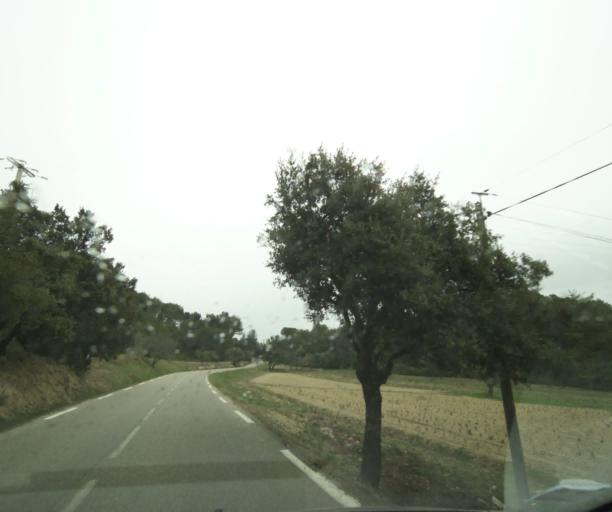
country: FR
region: Provence-Alpes-Cote d'Azur
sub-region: Departement des Bouches-du-Rhone
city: Saint-Marc-Jaumegarde
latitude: 43.5501
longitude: 5.5352
